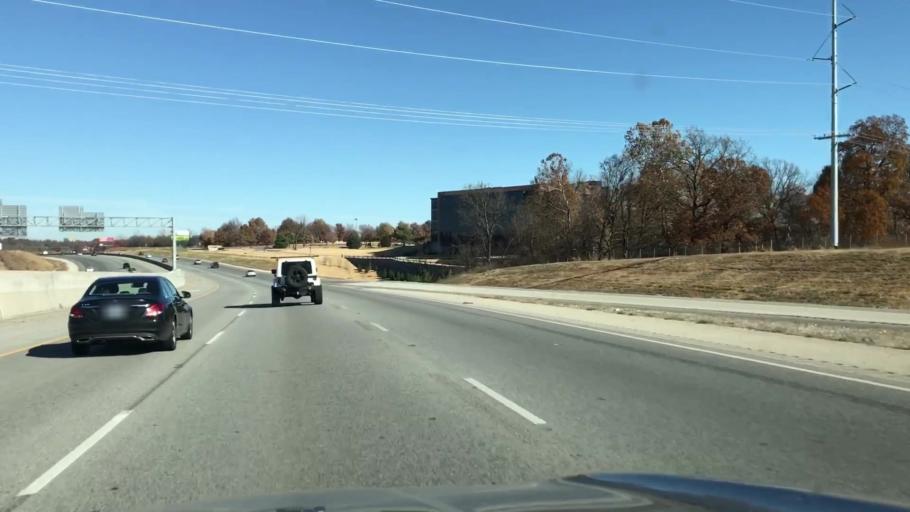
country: US
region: Arkansas
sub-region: Benton County
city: Lowell
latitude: 36.2423
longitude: -94.1529
